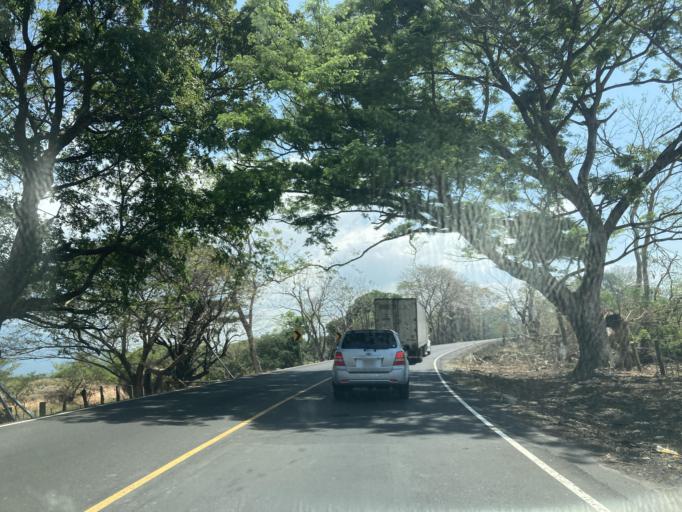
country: GT
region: Santa Rosa
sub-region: Municipio de Taxisco
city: Taxisco
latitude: 14.0954
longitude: -90.5737
